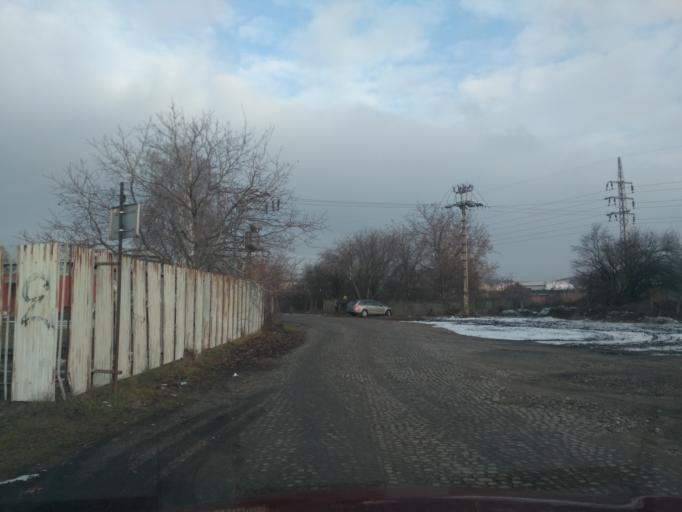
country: SK
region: Kosicky
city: Kosice
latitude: 48.7333
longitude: 21.2638
